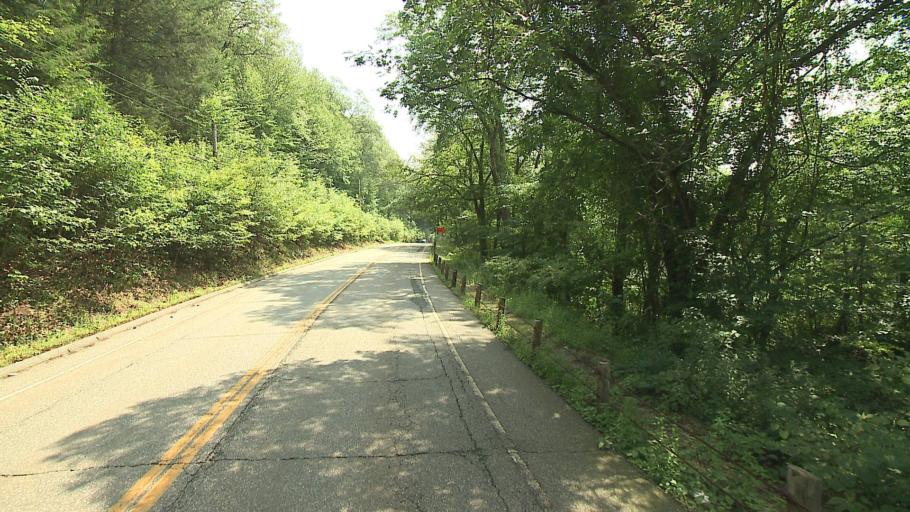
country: US
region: Connecticut
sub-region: Litchfield County
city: Oakville
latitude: 41.6177
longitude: -73.0575
